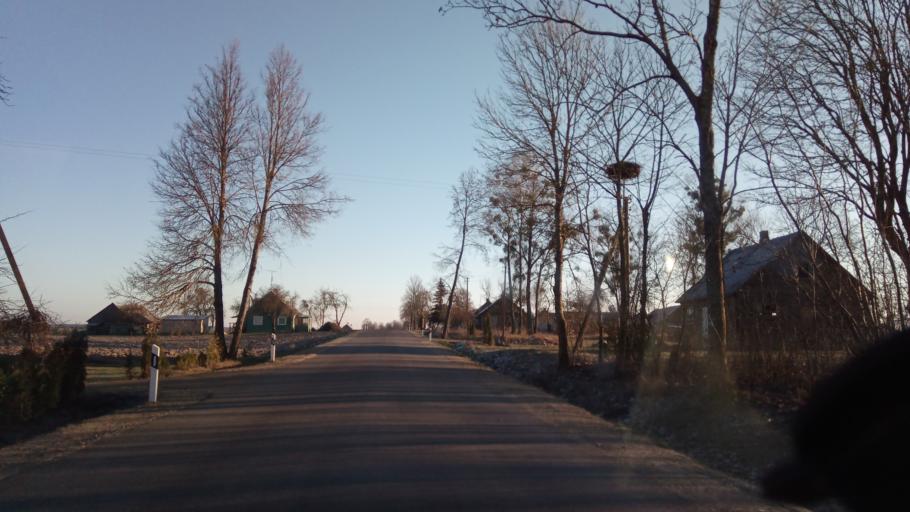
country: LT
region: Alytaus apskritis
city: Druskininkai
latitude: 54.1405
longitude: 23.9748
